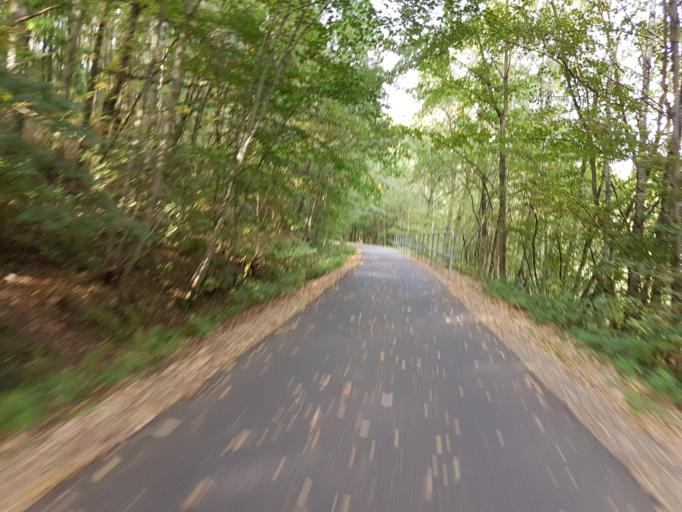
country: DE
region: Saxony
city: Wittgensdorf
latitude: 50.8997
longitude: 12.8960
